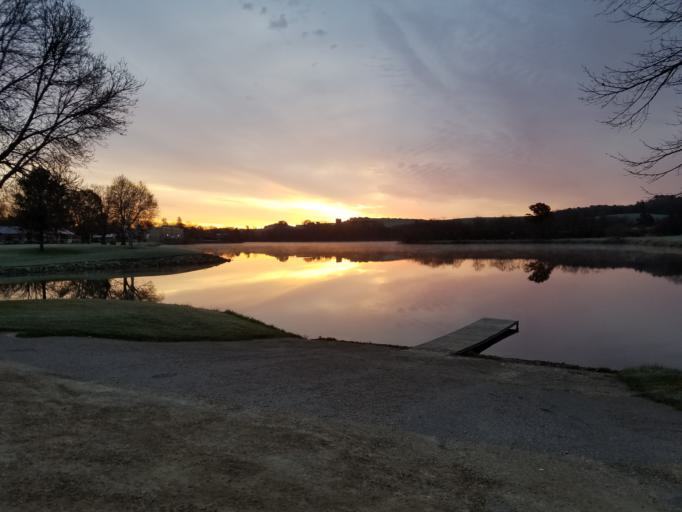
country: US
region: Wisconsin
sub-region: Vernon County
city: Hillsboro
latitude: 43.6479
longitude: -90.3510
